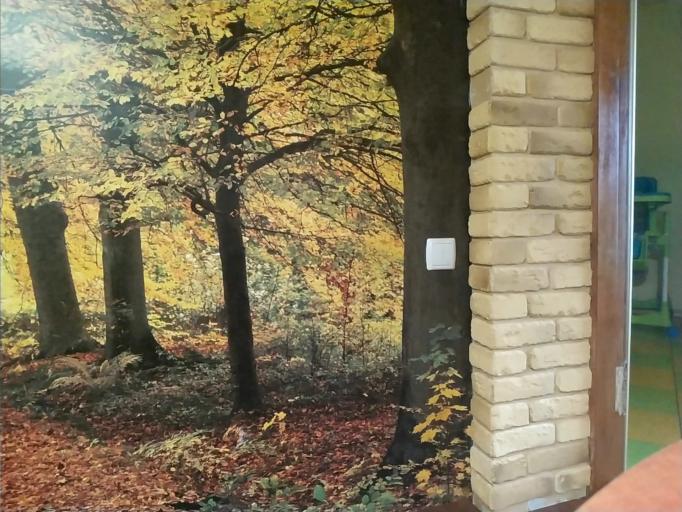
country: RU
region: Tverskaya
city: Likhoslavl'
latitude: 56.9474
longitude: 35.6278
